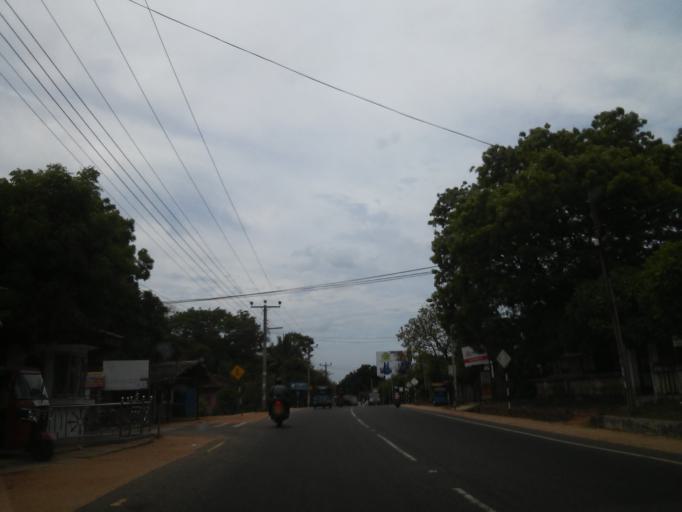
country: LK
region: Eastern Province
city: Trincomalee
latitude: 8.5866
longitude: 81.2114
